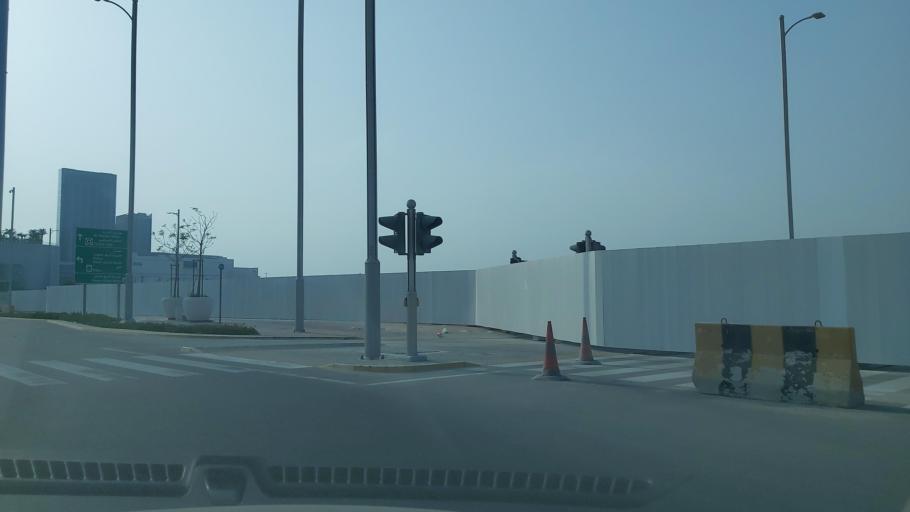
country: AE
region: Abu Dhabi
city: Abu Dhabi
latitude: 24.4982
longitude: 54.3987
